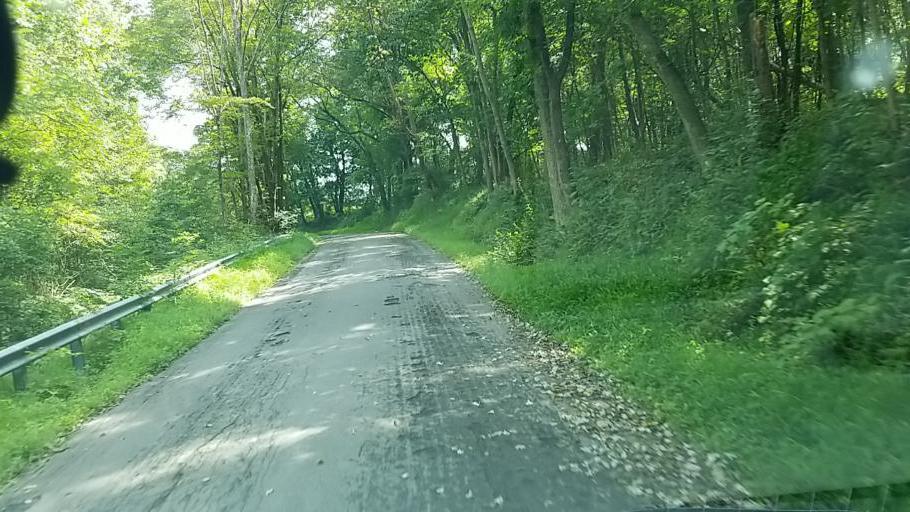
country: US
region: Pennsylvania
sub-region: Dauphin County
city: Elizabethville
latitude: 40.5442
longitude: -76.8641
